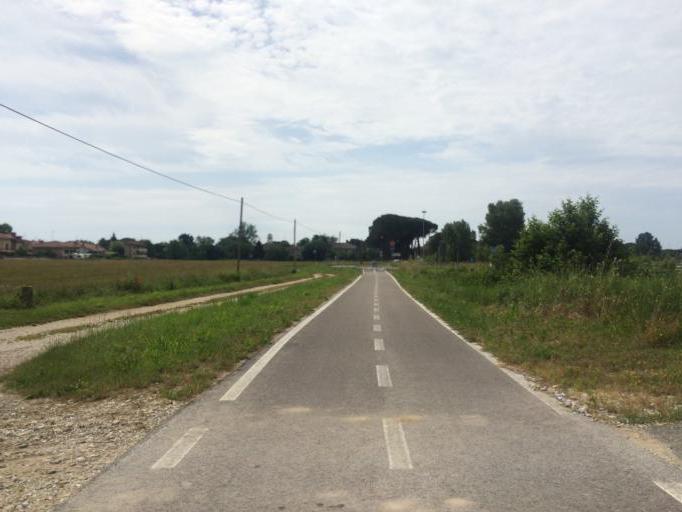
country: IT
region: Friuli Venezia Giulia
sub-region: Provincia di Udine
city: Aquileia
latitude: 45.7324
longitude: 13.3886
